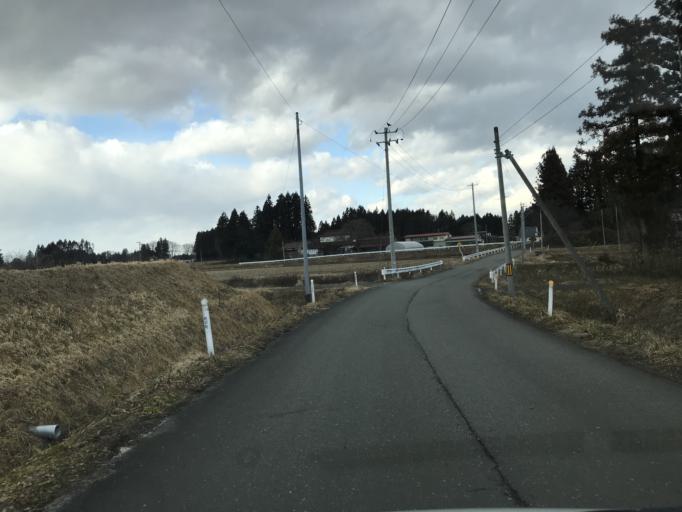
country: JP
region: Iwate
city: Mizusawa
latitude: 39.0805
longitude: 141.1113
